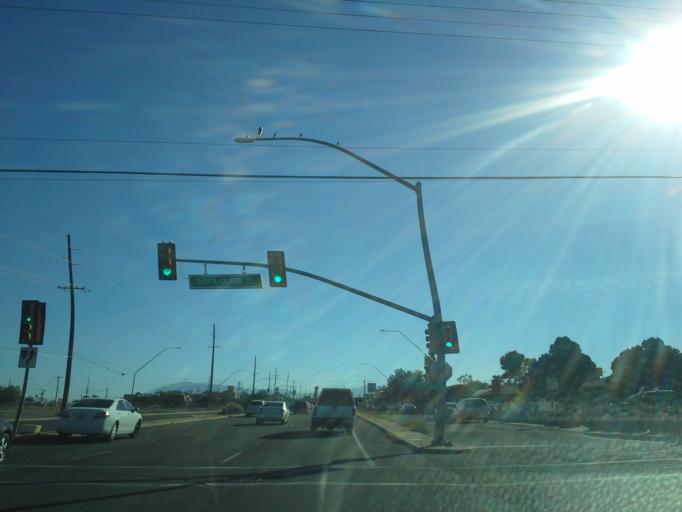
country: US
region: Arizona
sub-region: Pima County
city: Drexel Heights
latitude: 32.1338
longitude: -110.9821
